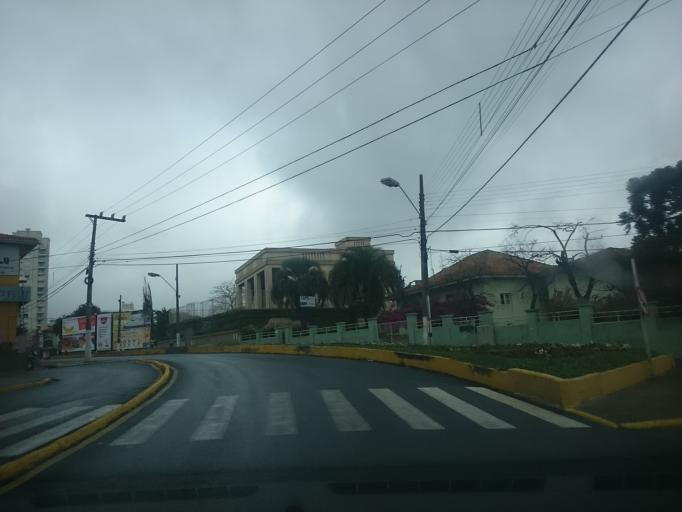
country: BR
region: Santa Catarina
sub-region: Lages
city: Lages
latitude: -27.8107
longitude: -50.3229
